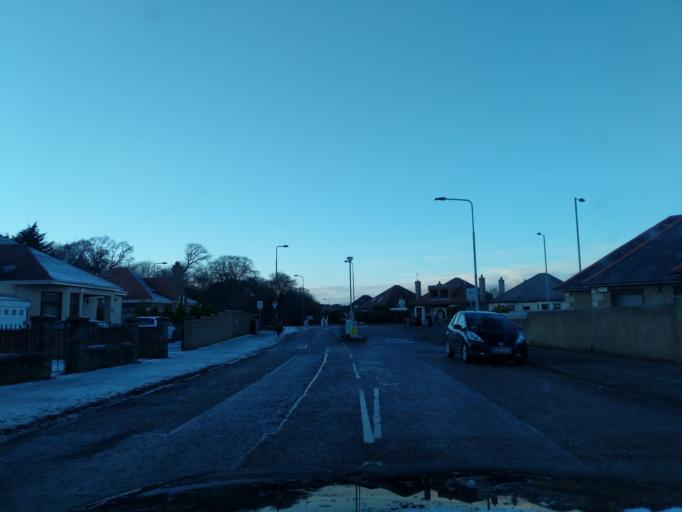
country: GB
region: Scotland
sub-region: West Lothian
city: Seafield
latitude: 55.9421
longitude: -3.1286
